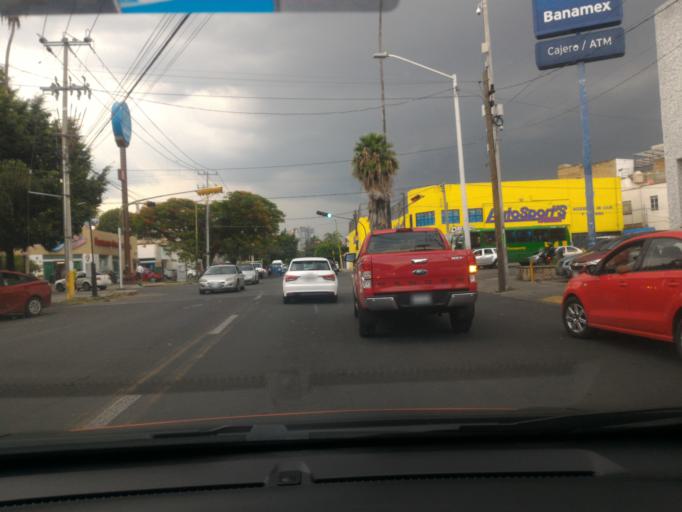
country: MX
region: Jalisco
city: Guadalajara
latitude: 20.6642
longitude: -103.3593
